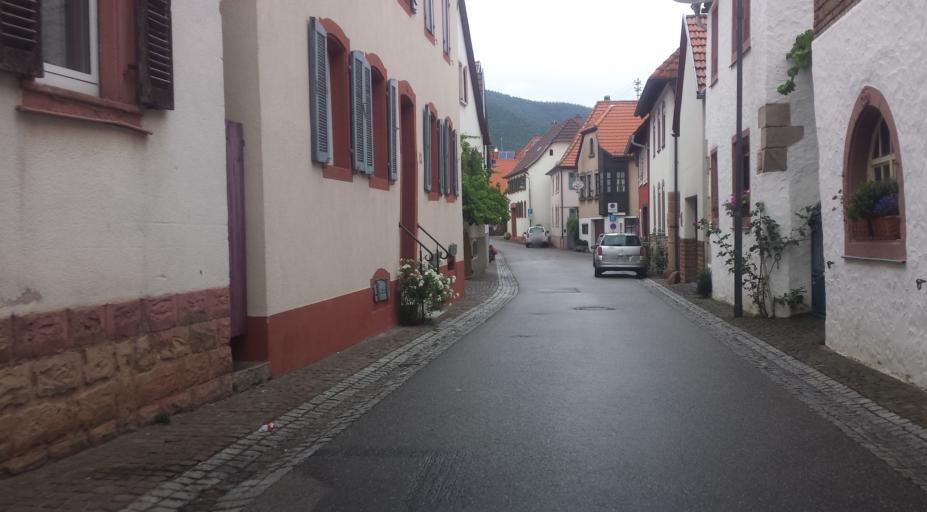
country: DE
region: Rheinland-Pfalz
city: Burrweiler
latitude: 49.2483
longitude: 8.0756
